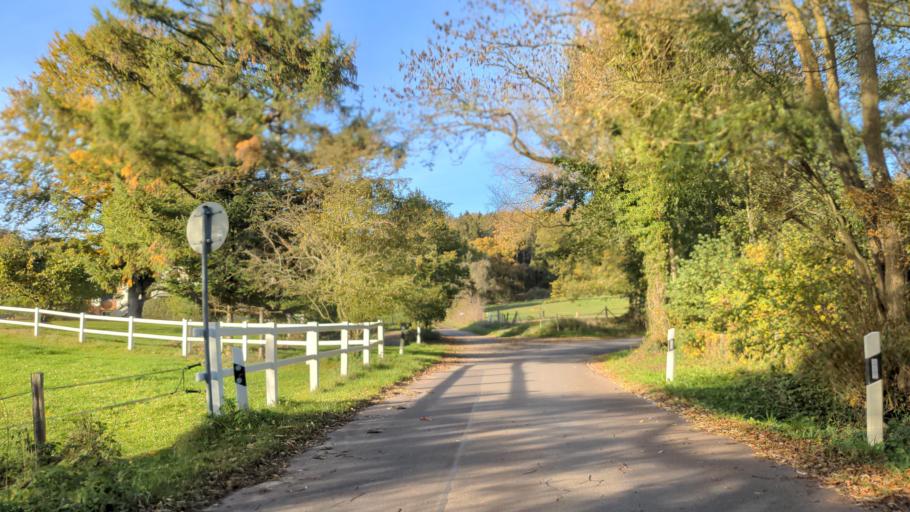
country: DE
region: Schleswig-Holstein
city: Kirchnuchel
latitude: 54.1897
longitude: 10.6755
